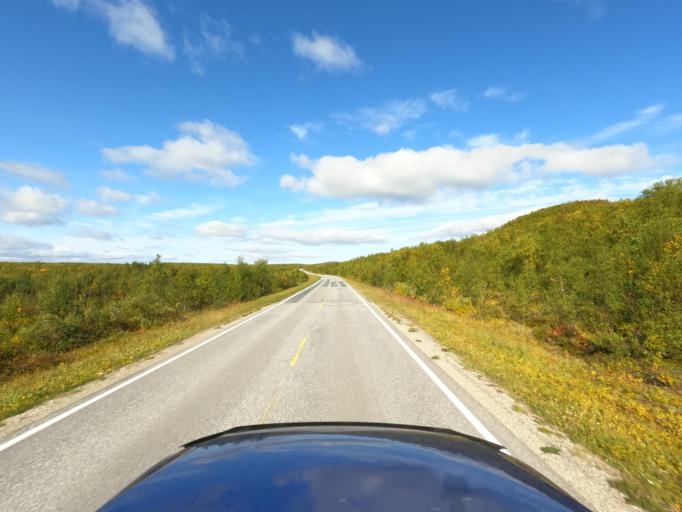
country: NO
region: Finnmark Fylke
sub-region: Karasjok
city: Karasjohka
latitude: 69.5398
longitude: 25.4296
